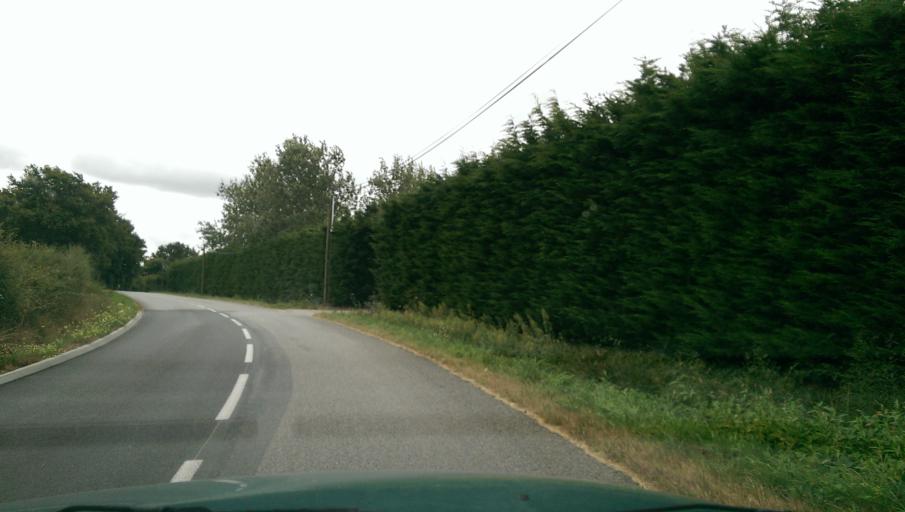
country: FR
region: Pays de la Loire
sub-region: Departement de la Loire-Atlantique
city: Remouille
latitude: 47.0473
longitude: -1.3908
